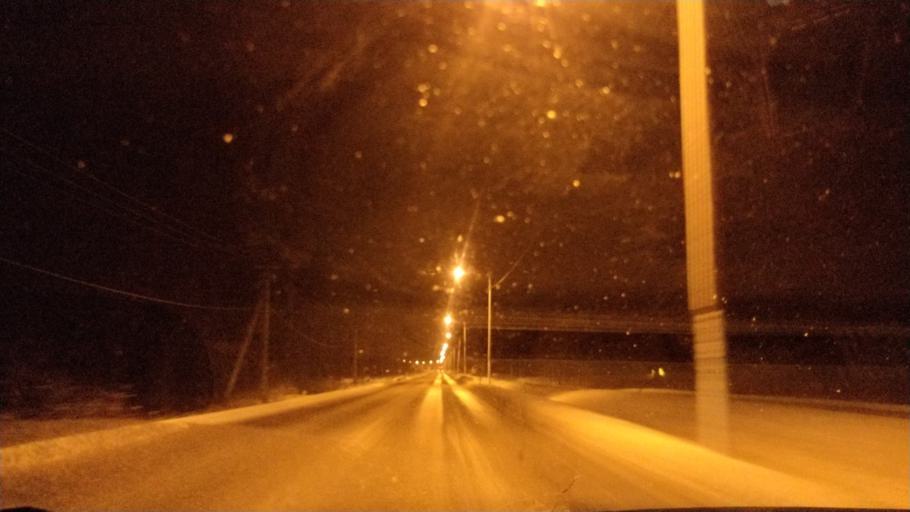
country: FI
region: Lapland
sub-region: Rovaniemi
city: Rovaniemi
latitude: 66.3086
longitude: 25.3605
